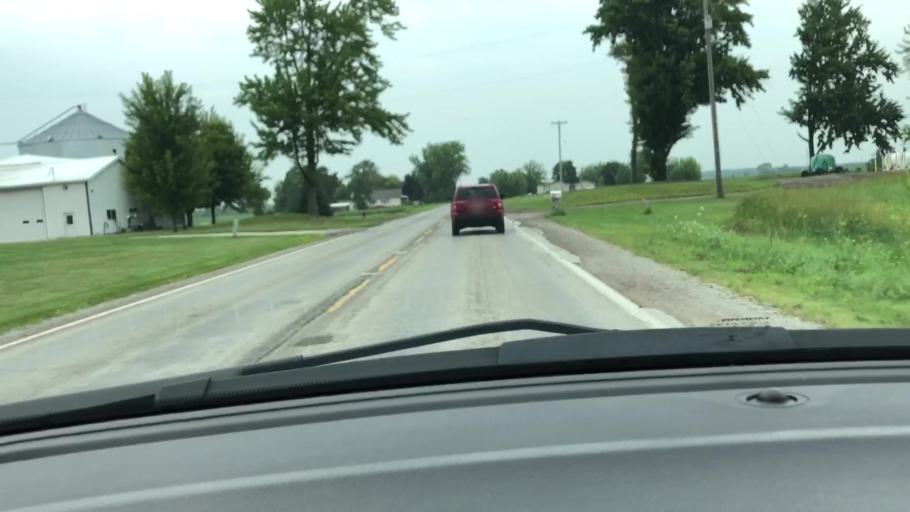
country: US
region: Michigan
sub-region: Saginaw County
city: Freeland
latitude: 43.5473
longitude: -84.0902
